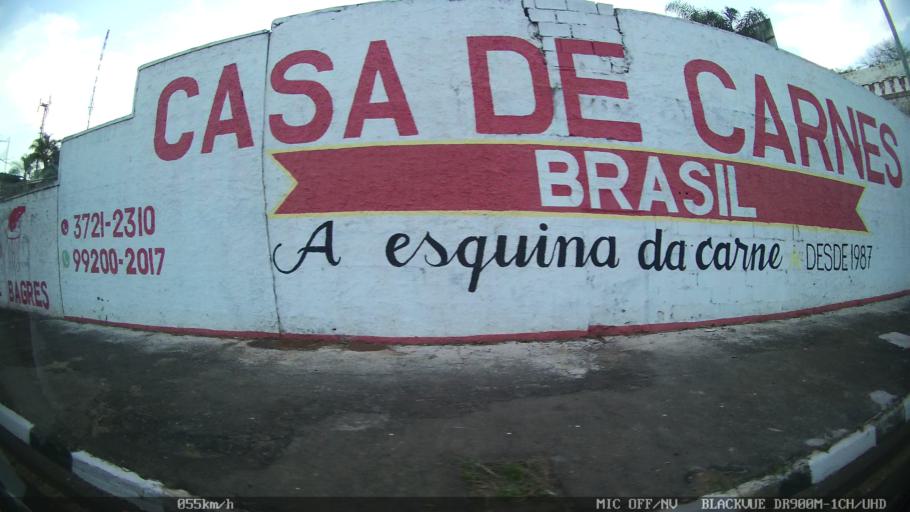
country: BR
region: Sao Paulo
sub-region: Franca
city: Franca
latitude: -20.5336
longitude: -47.4056
